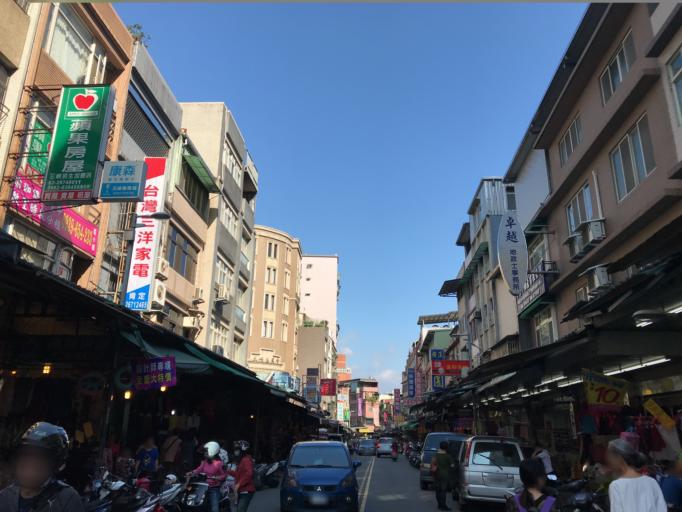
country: TW
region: Taiwan
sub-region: Taoyuan
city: Taoyuan
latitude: 24.9348
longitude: 121.3712
